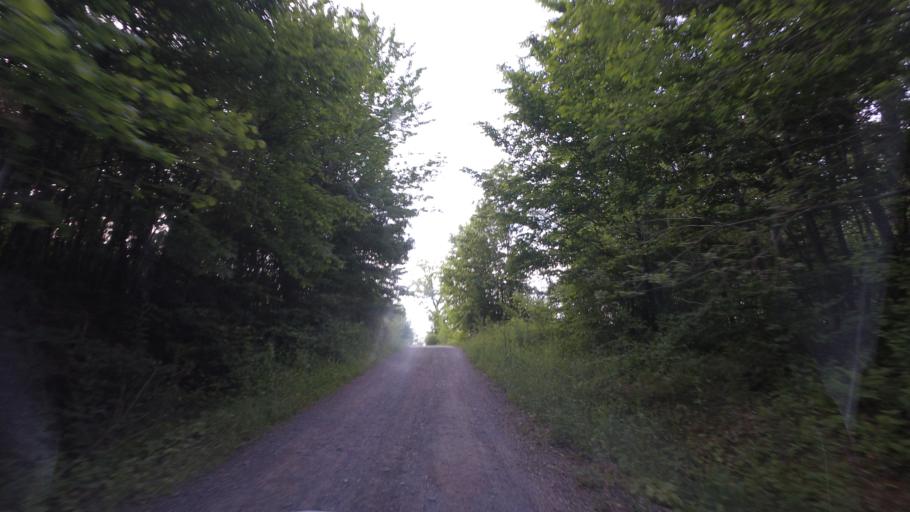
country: HR
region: Sisacko-Moslavacka
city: Gvozd
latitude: 45.3091
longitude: 15.9783
